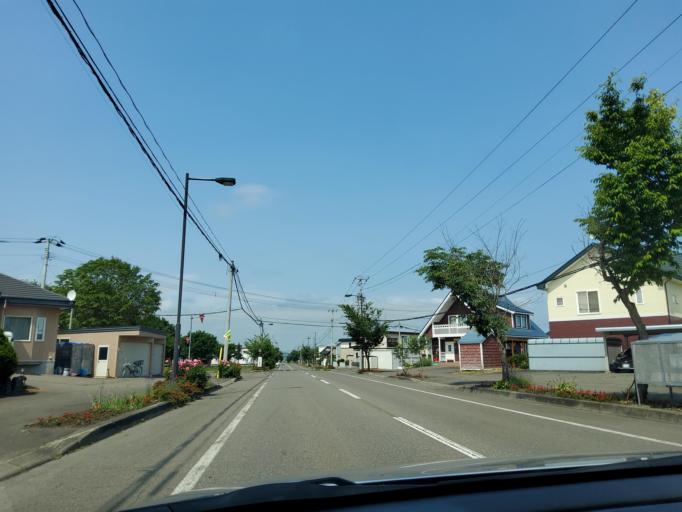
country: JP
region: Hokkaido
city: Obihiro
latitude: 42.9002
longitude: 143.0473
